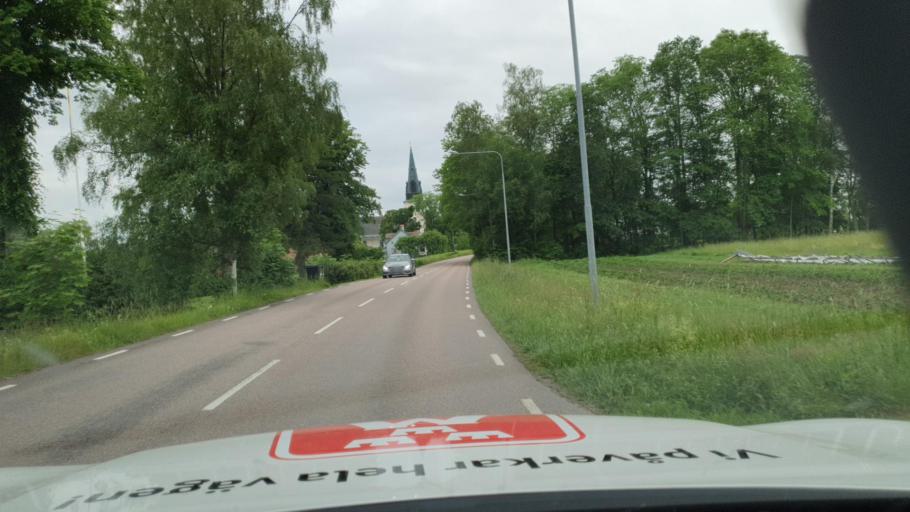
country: SE
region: Vaermland
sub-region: Kils Kommun
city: Kil
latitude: 59.5305
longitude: 13.3155
